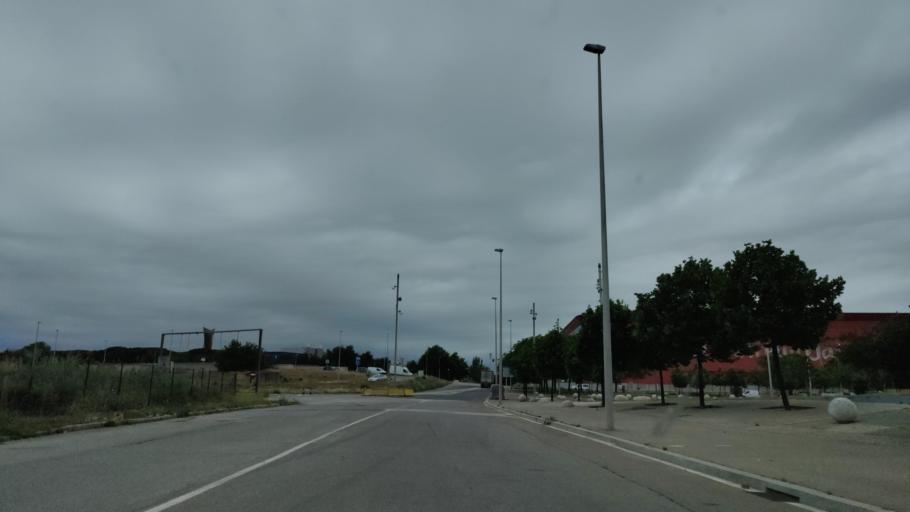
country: ES
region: Catalonia
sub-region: Provincia de Barcelona
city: El Prat de Llobregat
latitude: 41.3155
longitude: 2.0805
